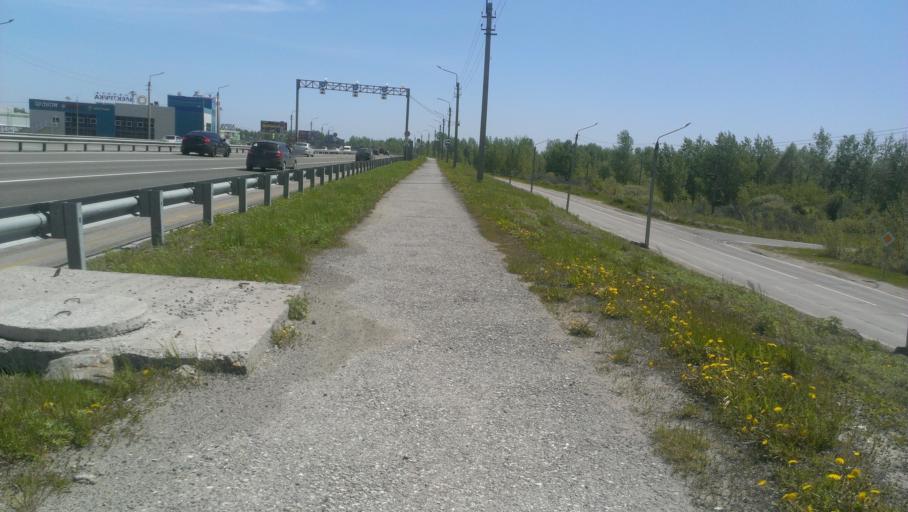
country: RU
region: Altai Krai
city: Zaton
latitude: 53.3171
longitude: 83.8217
